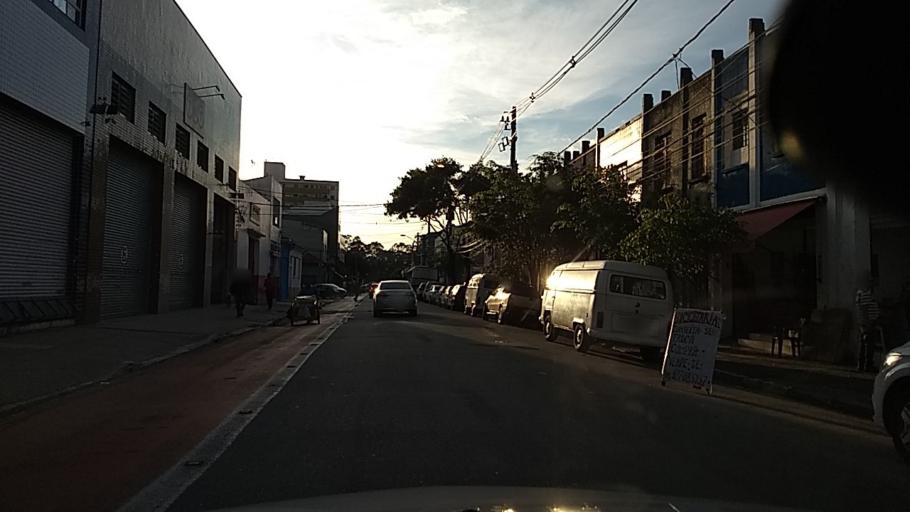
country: BR
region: Sao Paulo
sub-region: Sao Paulo
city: Sao Paulo
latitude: -23.5274
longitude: -46.6191
